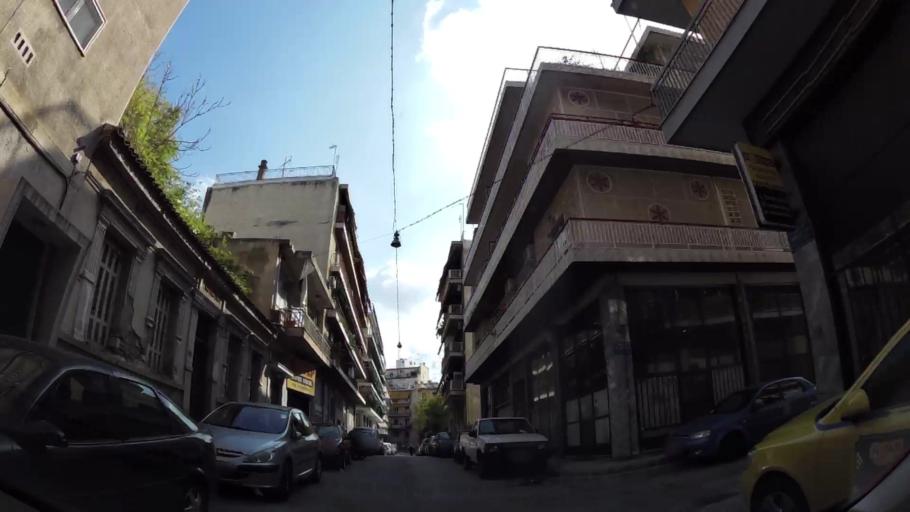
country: GR
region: Attica
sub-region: Nomarchia Athinas
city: Dhafni
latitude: 37.9653
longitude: 23.7316
